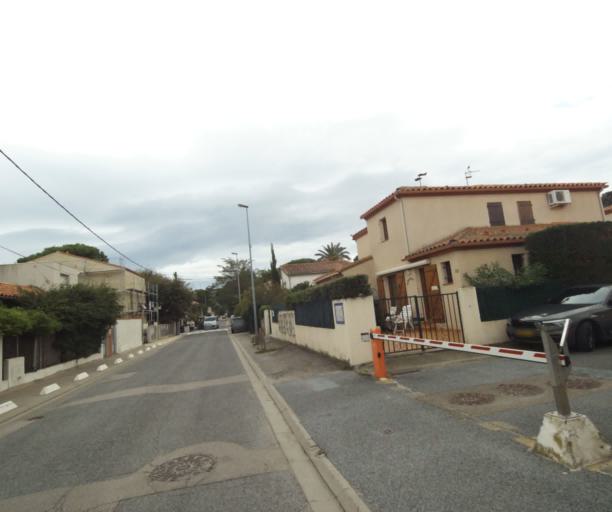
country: FR
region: Languedoc-Roussillon
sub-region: Departement des Pyrenees-Orientales
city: Argelers
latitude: 42.5383
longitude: 3.0533
